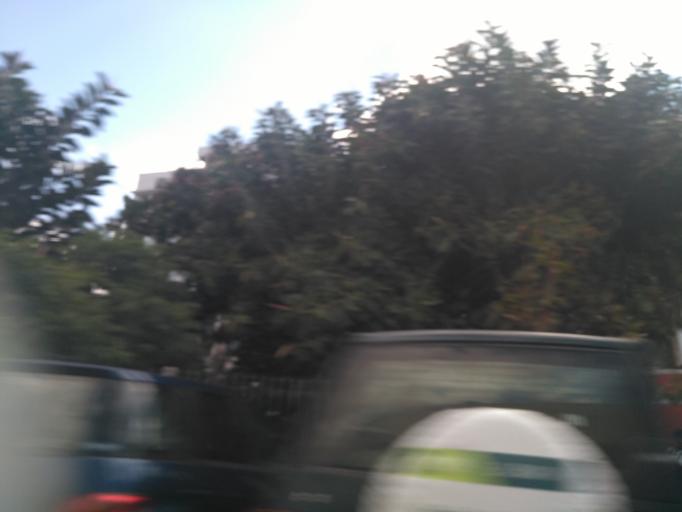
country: TZ
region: Mwanza
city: Mwanza
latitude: -2.5194
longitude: 32.8997
